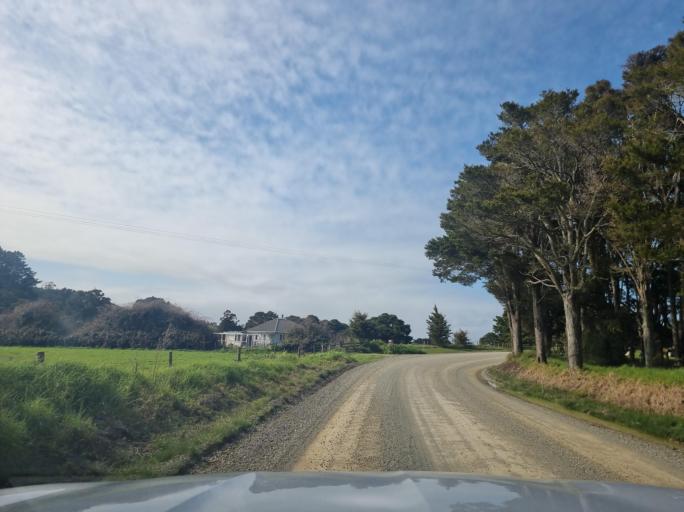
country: NZ
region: Auckland
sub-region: Auckland
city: Wellsford
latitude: -36.1064
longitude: 174.5009
